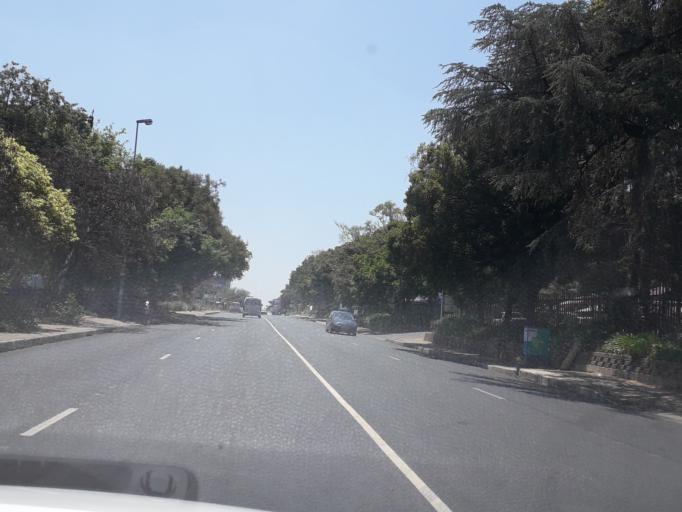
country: ZA
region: Gauteng
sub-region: City of Johannesburg Metropolitan Municipality
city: Johannesburg
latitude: -26.0979
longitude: 27.9994
